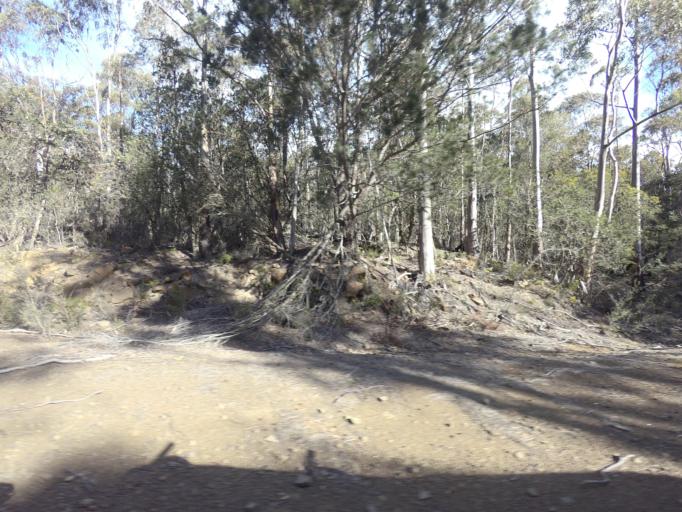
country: AU
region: Tasmania
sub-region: Break O'Day
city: St Helens
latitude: -41.8380
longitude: 148.0621
